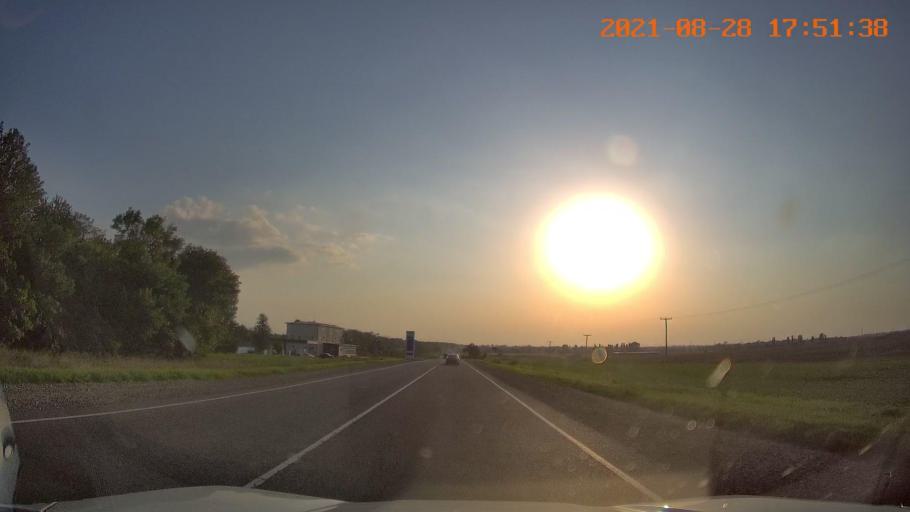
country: RU
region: Krasnodarskiy
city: Konstantinovskaya
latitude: 44.9431
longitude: 40.7888
